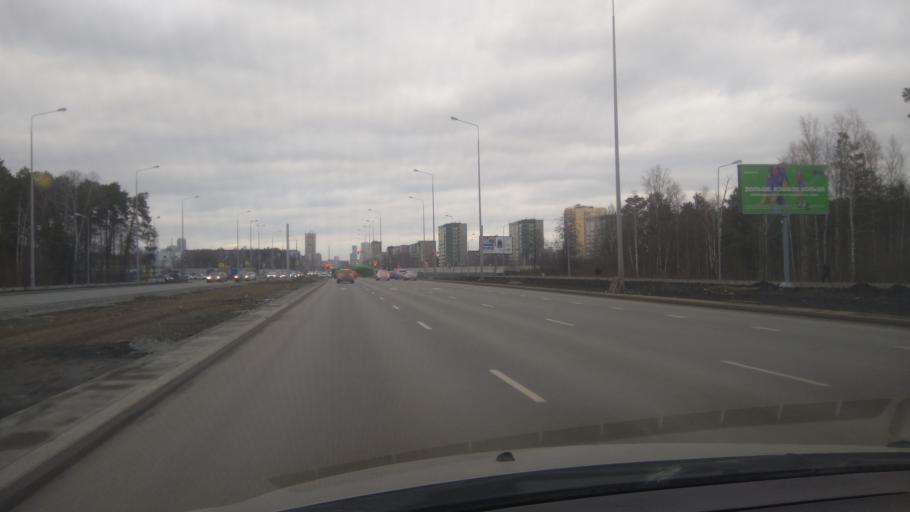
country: RU
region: Sverdlovsk
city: Sovkhoznyy
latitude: 56.8018
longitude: 60.5362
